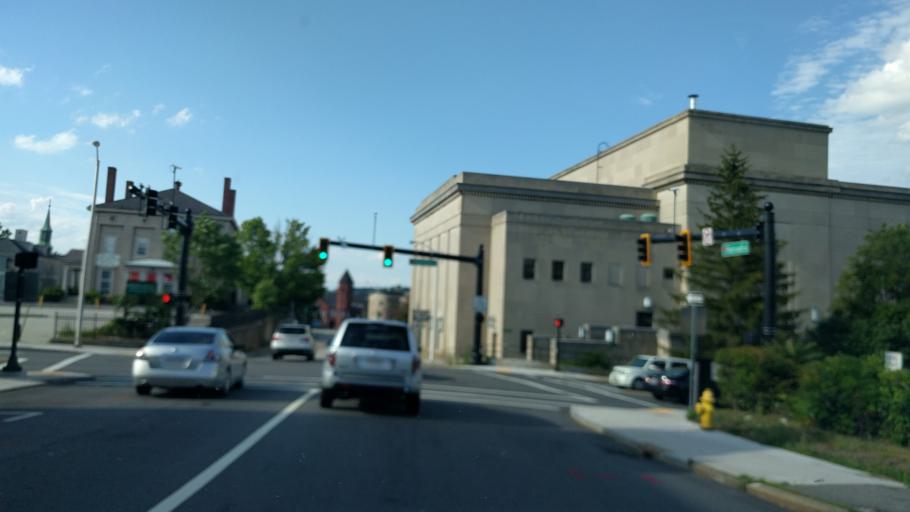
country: US
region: Massachusetts
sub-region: Worcester County
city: Worcester
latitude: 42.2712
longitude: -71.8018
